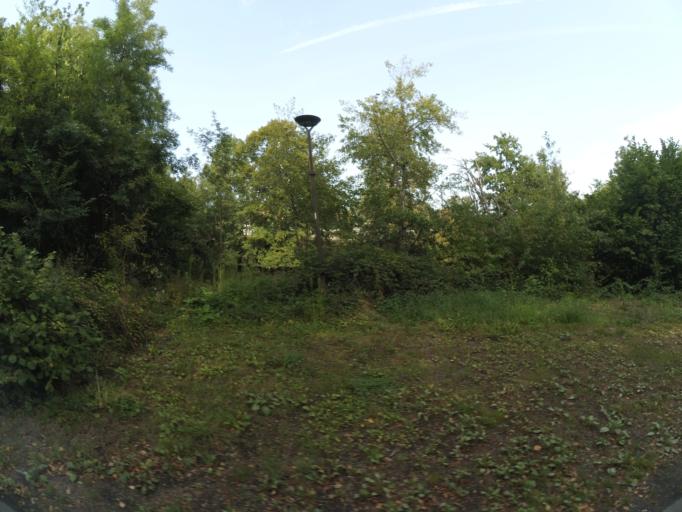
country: FR
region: Pays de la Loire
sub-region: Departement de la Vendee
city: Saint-Georges-de-Montaigu
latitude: 46.9461
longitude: -1.3015
